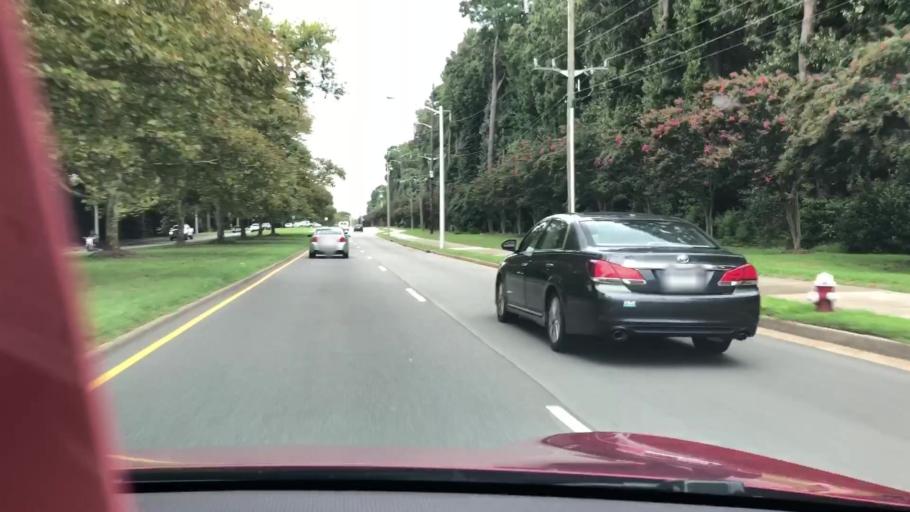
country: US
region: Virginia
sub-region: City of Virginia Beach
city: Virginia Beach
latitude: 36.8905
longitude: -76.0531
